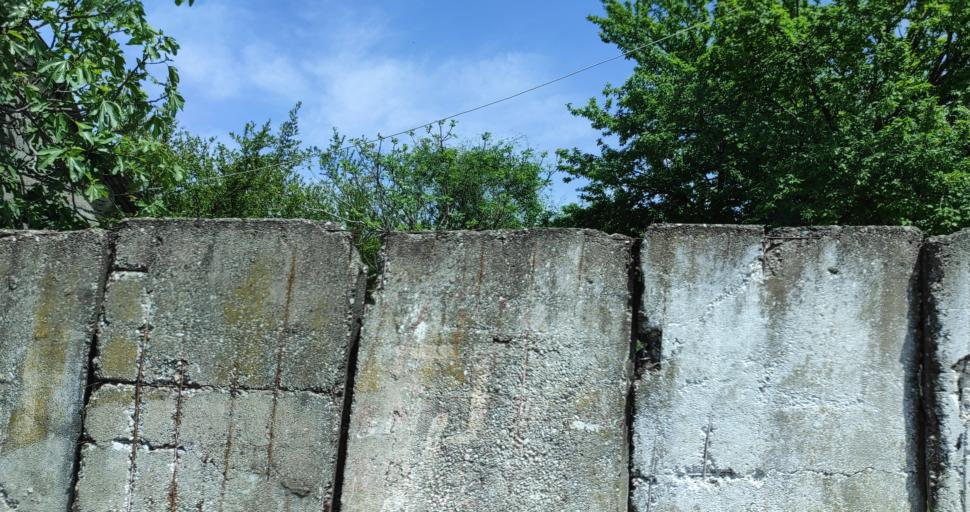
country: AL
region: Shkoder
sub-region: Rrethi i Malesia e Madhe
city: Gruemire
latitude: 42.1470
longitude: 19.5423
